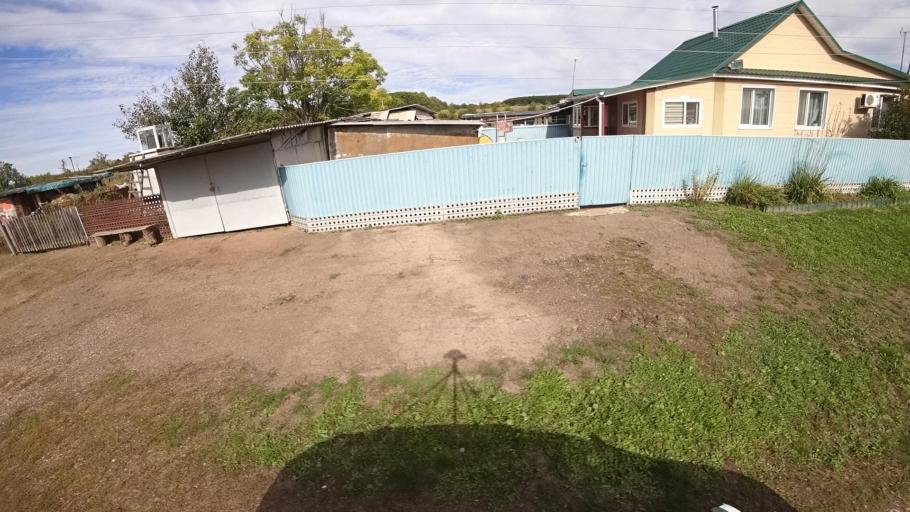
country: RU
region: Primorskiy
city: Dostoyevka
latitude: 44.3190
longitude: 133.4776
